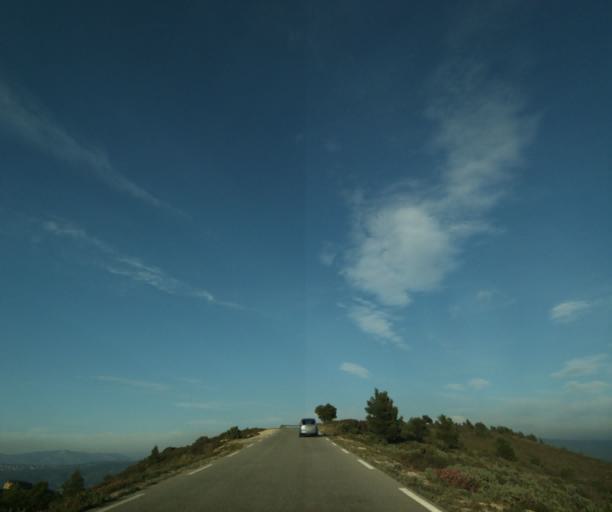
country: FR
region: Provence-Alpes-Cote d'Azur
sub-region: Departement des Bouches-du-Rhone
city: Cassis
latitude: 43.1998
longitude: 5.5542
